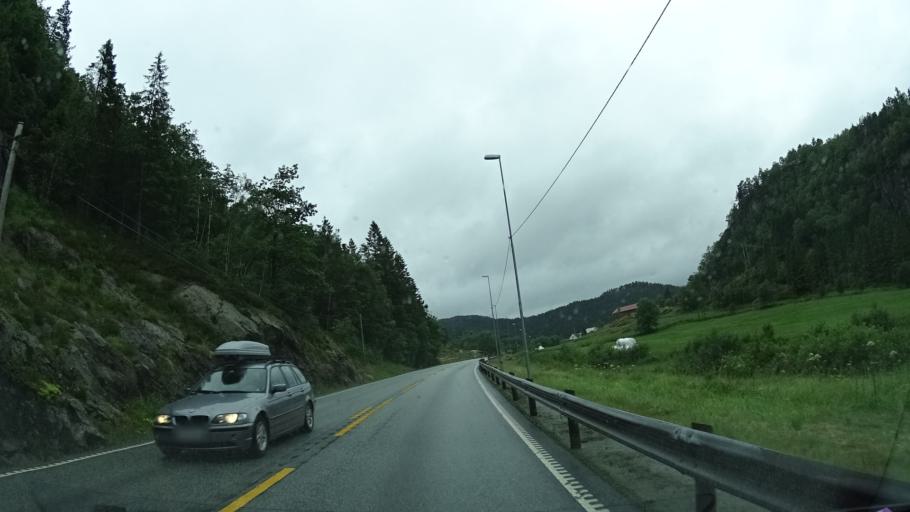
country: NO
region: Vest-Agder
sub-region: Flekkefjord
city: Flekkefjord
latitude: 58.3644
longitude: 6.6355
